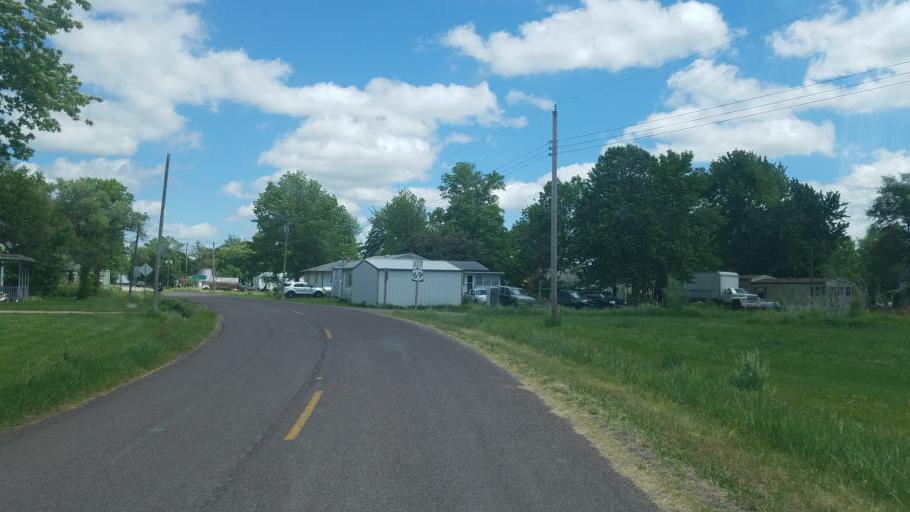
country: US
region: Iowa
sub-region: Decatur County
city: Lamoni
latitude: 40.4709
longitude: -93.9910
